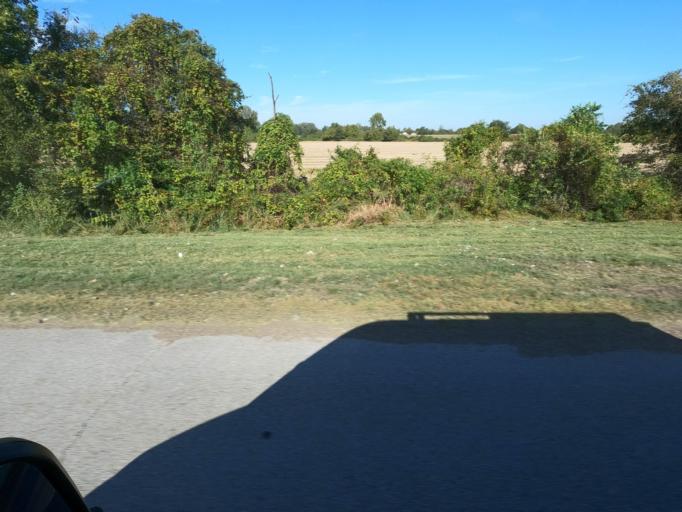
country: US
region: Tennessee
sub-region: Shelby County
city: Millington
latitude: 35.3728
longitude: -89.8793
